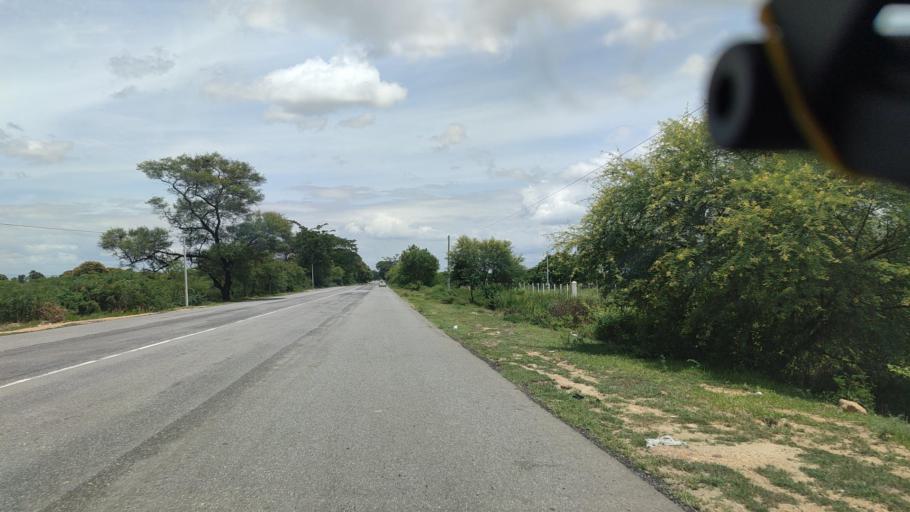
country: MM
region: Mandalay
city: Meiktila
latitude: 20.6808
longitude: 95.9950
